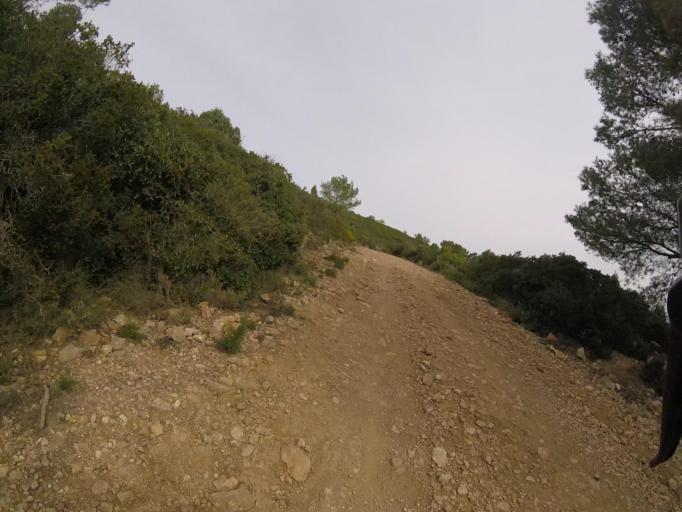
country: ES
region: Valencia
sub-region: Provincia de Castello
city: Benicassim
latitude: 40.0855
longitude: 0.0383
